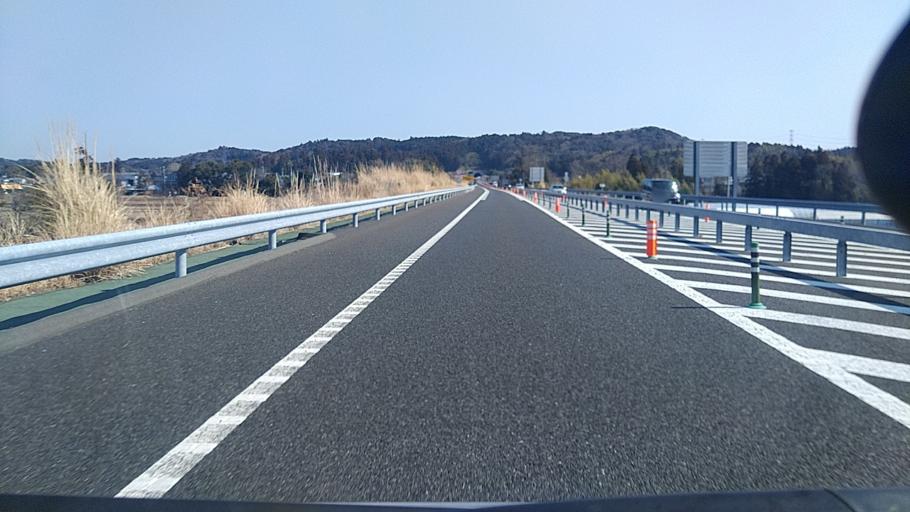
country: JP
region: Chiba
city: Kisarazu
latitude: 35.3593
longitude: 140.0539
